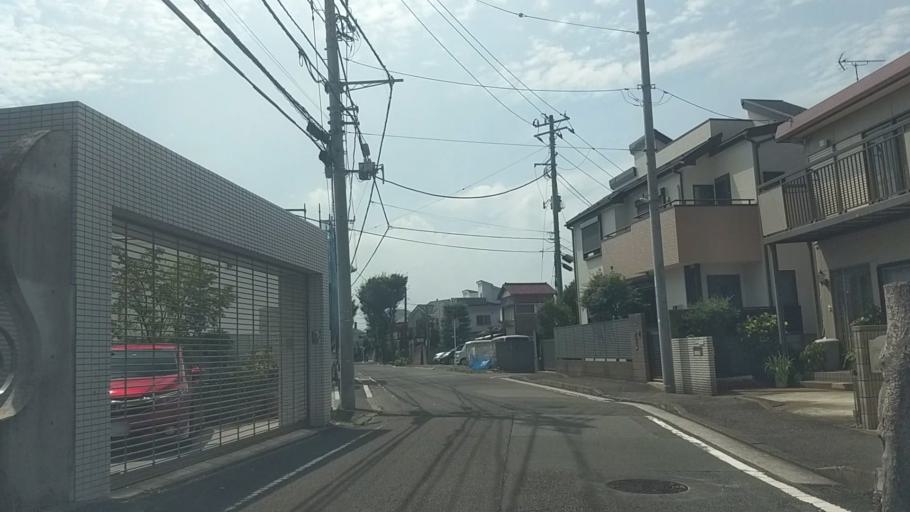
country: JP
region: Kanagawa
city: Yokohama
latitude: 35.4874
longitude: 139.6333
